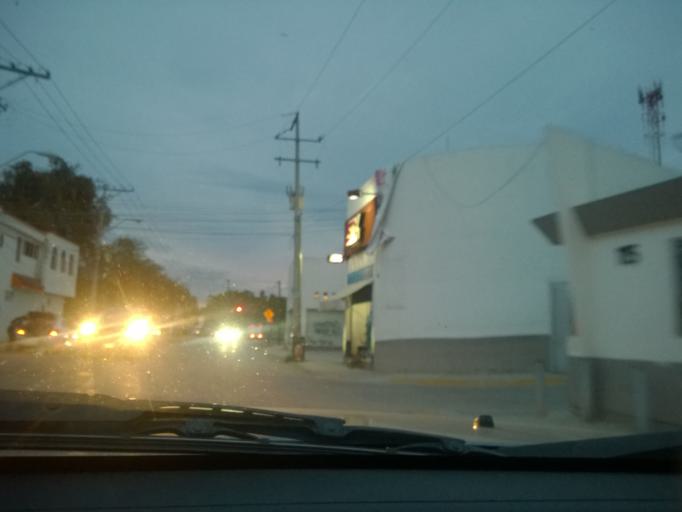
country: MX
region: Guanajuato
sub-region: Leon
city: Medina
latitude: 21.1277
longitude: -101.6379
